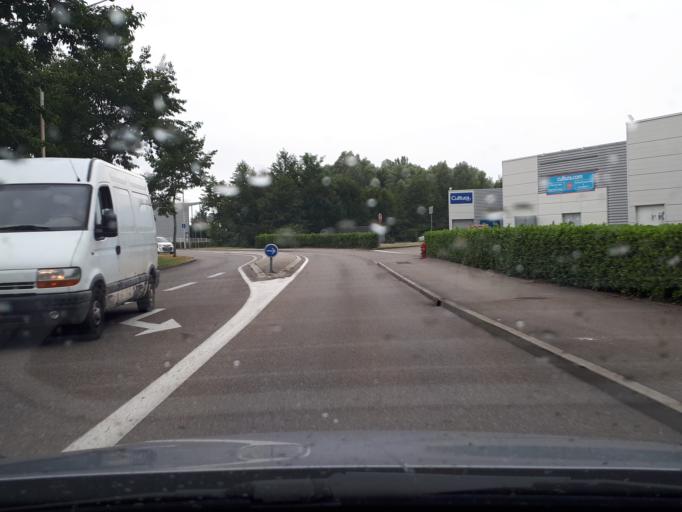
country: FR
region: Rhone-Alpes
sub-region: Departement de l'Isere
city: Domarin
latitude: 45.5898
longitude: 5.2518
